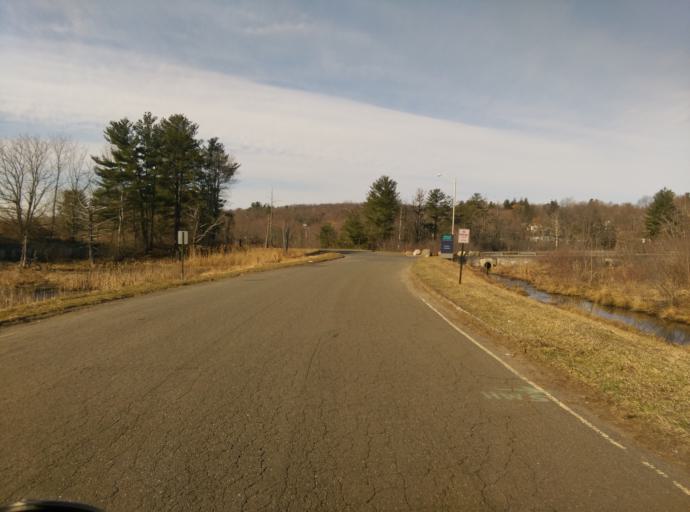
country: US
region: Massachusetts
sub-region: Essex County
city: Haverhill
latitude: 42.7880
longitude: -71.1234
